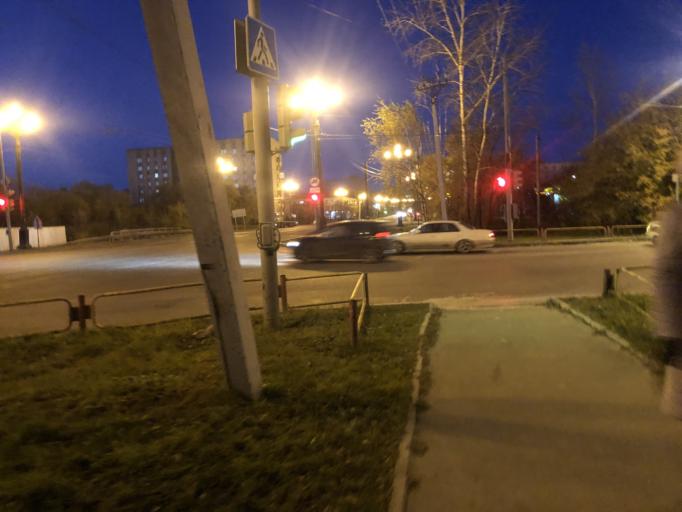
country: RU
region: Khabarovsk Krai
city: Topolevo
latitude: 48.5168
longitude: 135.1542
